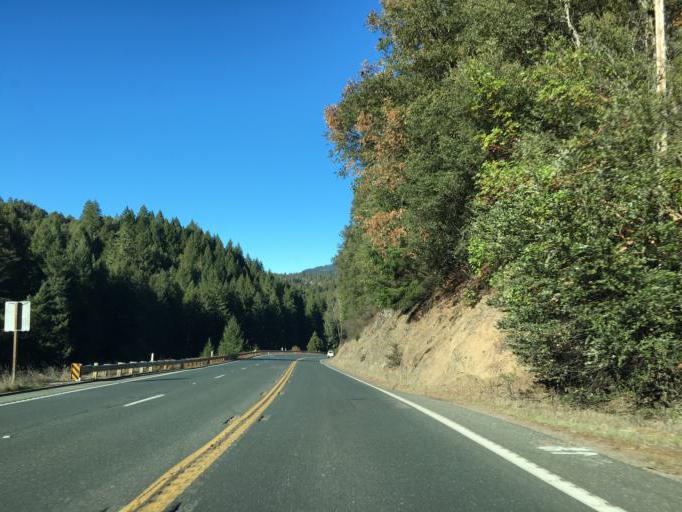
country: US
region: California
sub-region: Mendocino County
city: Brooktrails
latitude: 39.4752
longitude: -123.3635
